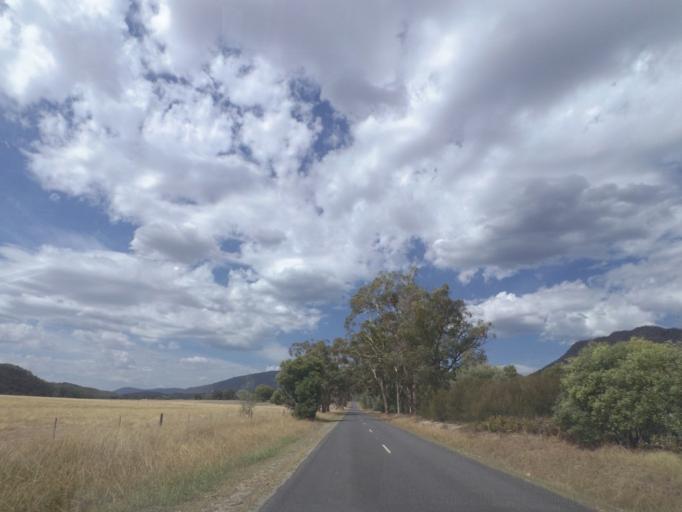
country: AU
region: Victoria
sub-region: Murrindindi
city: Alexandra
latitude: -37.3402
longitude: 145.7200
